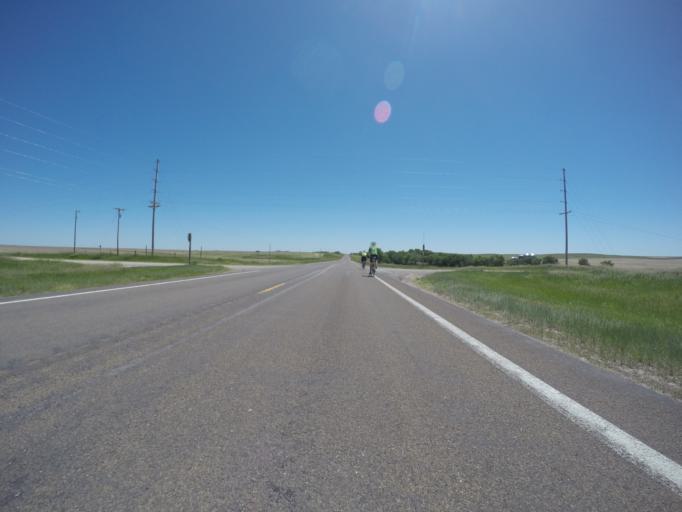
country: US
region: Kansas
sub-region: Norton County
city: Norton
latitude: 39.8285
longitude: -99.6092
